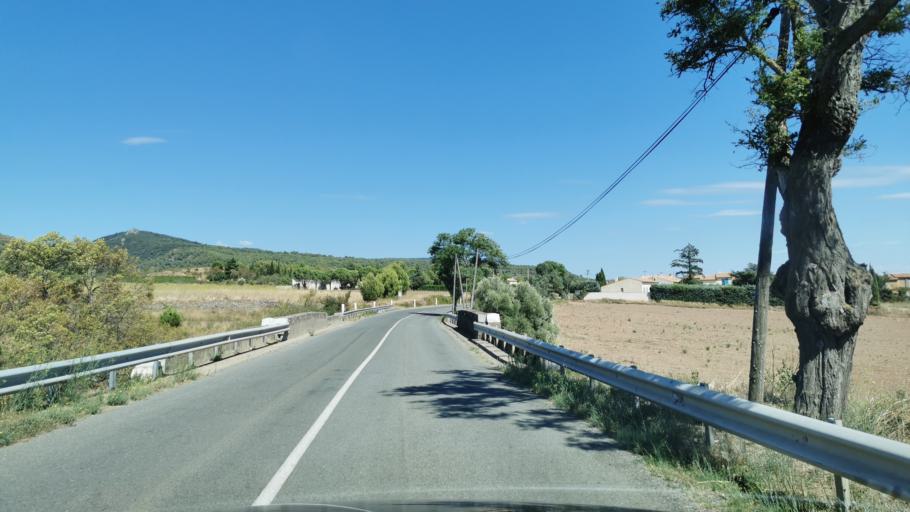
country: FR
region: Languedoc-Roussillon
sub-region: Departement de l'Aude
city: Caunes-Minervois
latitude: 43.3230
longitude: 2.5149
